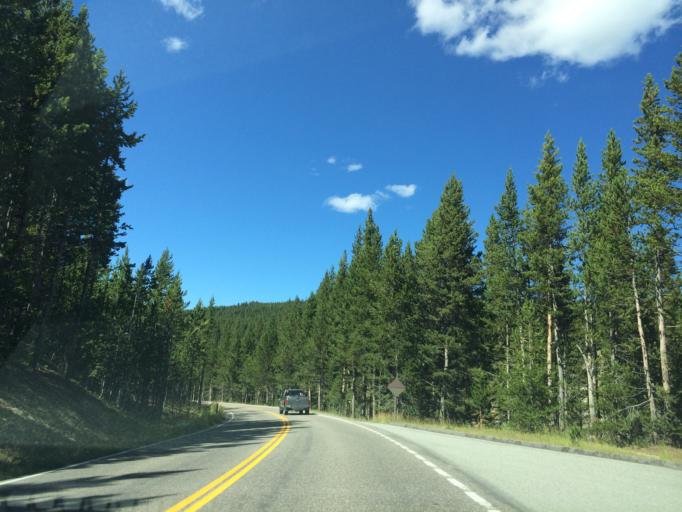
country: US
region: Montana
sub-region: Gallatin County
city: West Yellowstone
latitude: 44.6060
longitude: -110.3838
